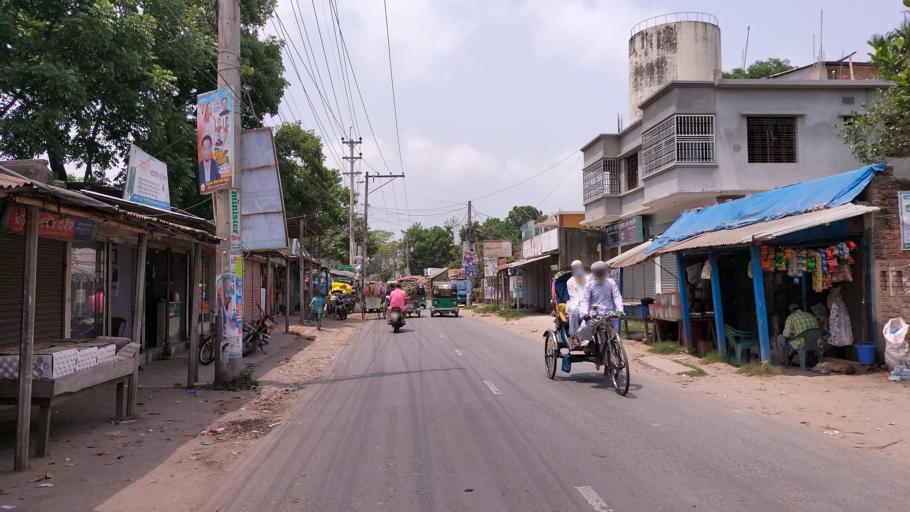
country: BD
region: Dhaka
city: Azimpur
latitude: 23.7299
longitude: 90.2797
